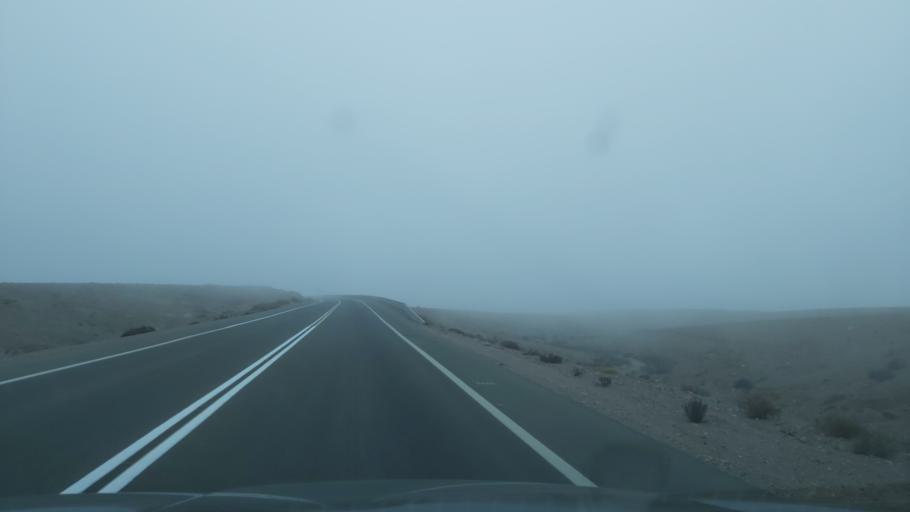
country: CL
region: Atacama
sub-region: Provincia de Copiapo
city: Copiapo
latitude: -27.2800
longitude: -70.0888
